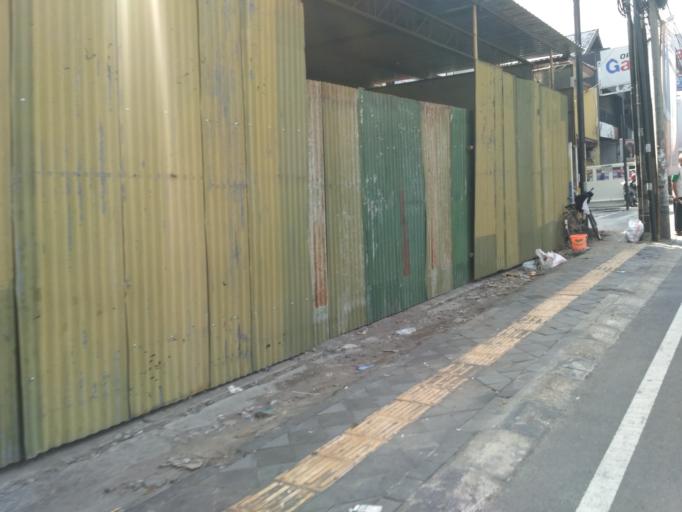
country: ID
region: Daerah Istimewa Yogyakarta
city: Depok
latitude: -7.7689
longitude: 110.4100
